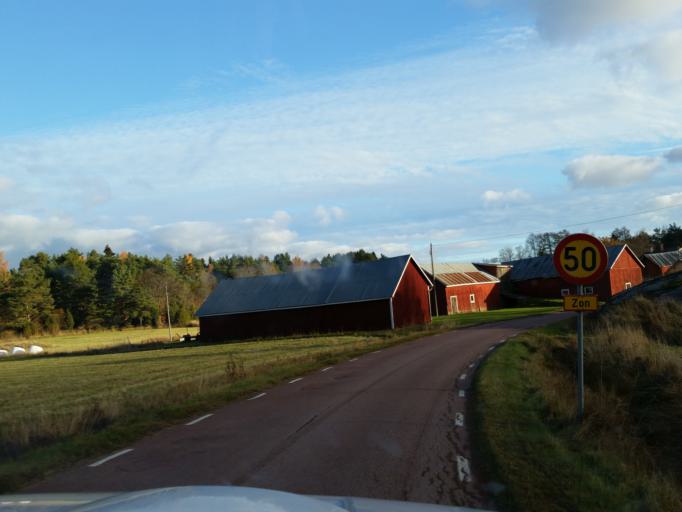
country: AX
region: Alands skaergard
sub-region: Foegloe
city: Foegloe
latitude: 60.0007
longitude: 20.3540
